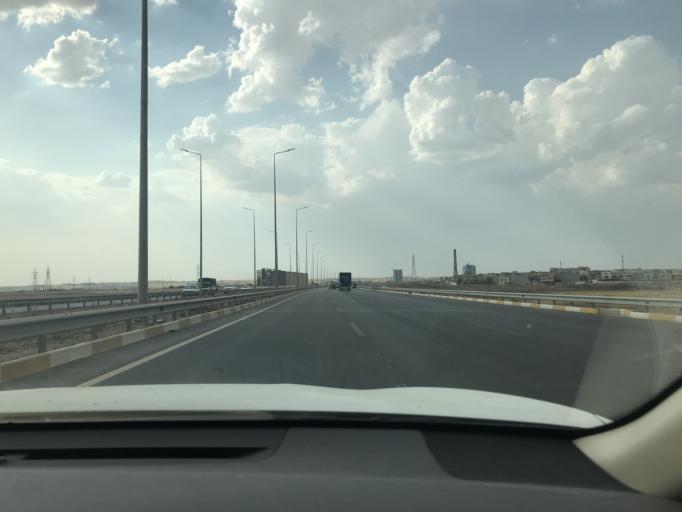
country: IQ
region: Arbil
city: Erbil
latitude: 36.1578
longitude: 43.9594
